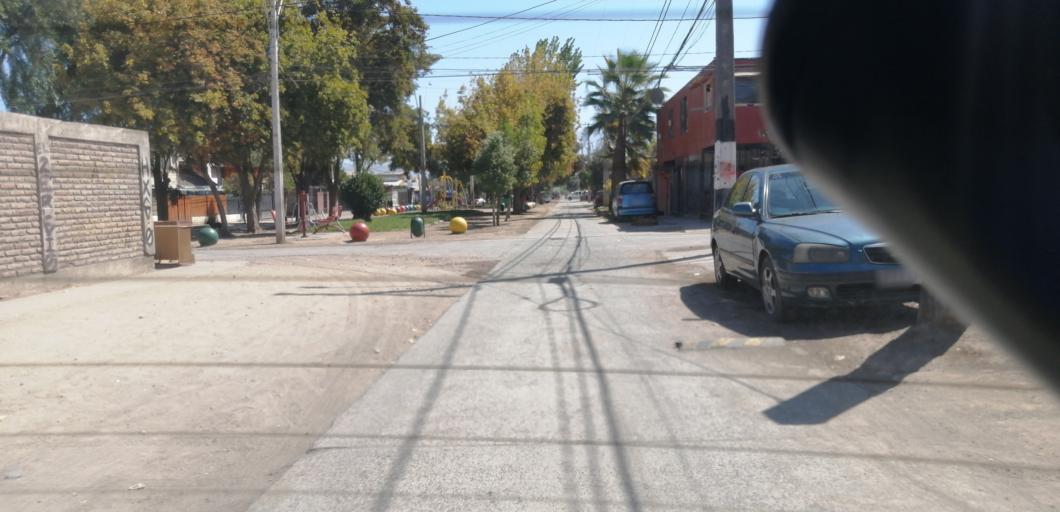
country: CL
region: Santiago Metropolitan
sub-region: Provincia de Santiago
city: Lo Prado
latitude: -33.4492
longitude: -70.7460
